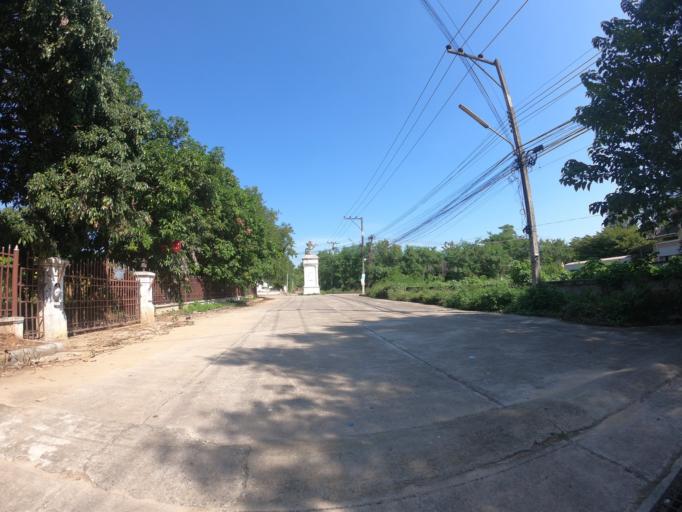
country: TH
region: Chiang Mai
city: Chiang Mai
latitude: 18.8058
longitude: 99.0079
